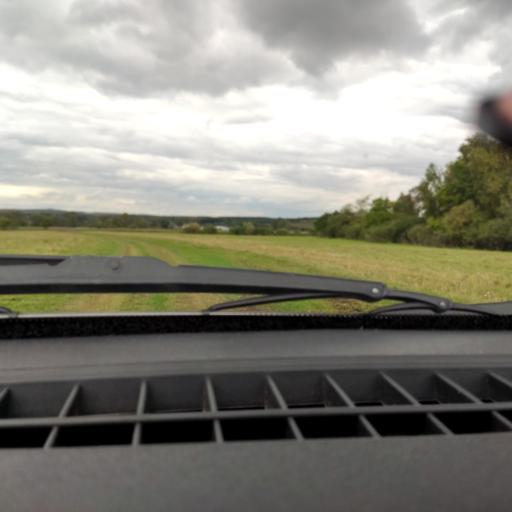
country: RU
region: Bashkortostan
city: Iglino
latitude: 54.7043
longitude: 56.4048
